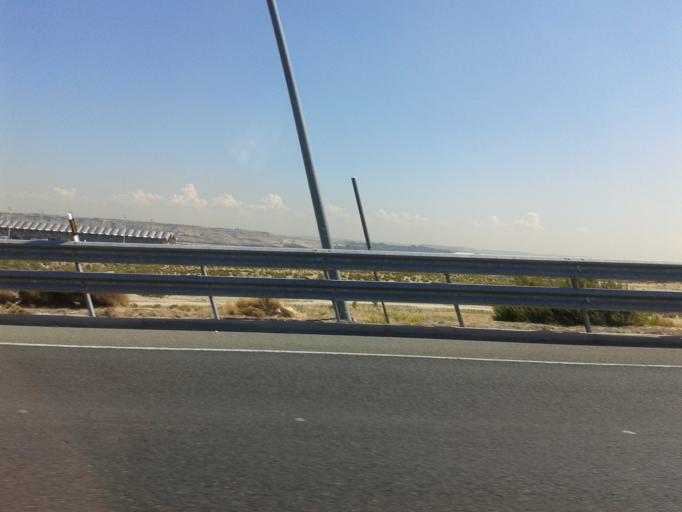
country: ES
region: Madrid
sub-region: Provincia de Madrid
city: Barajas de Madrid
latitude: 40.4844
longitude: -3.6011
